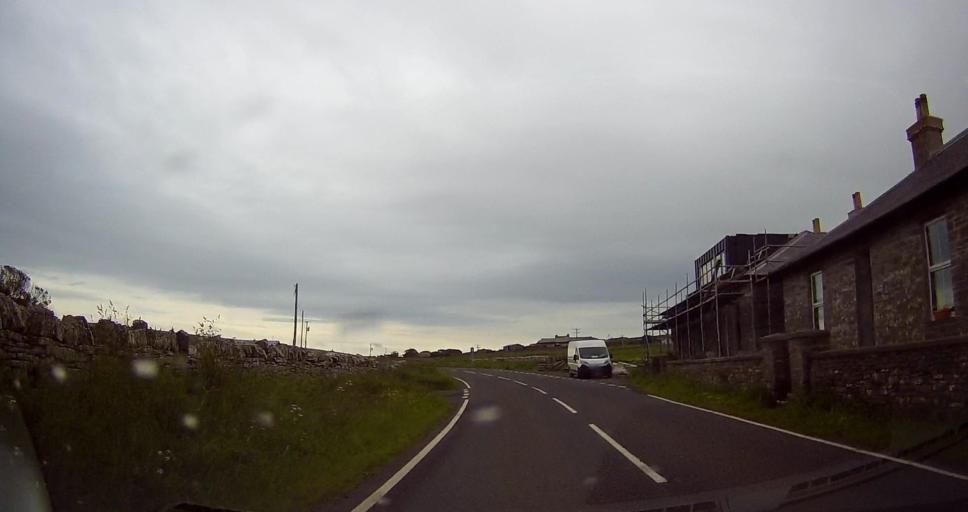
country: GB
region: Scotland
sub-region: Orkney Islands
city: Orkney
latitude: 59.1107
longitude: -3.1000
